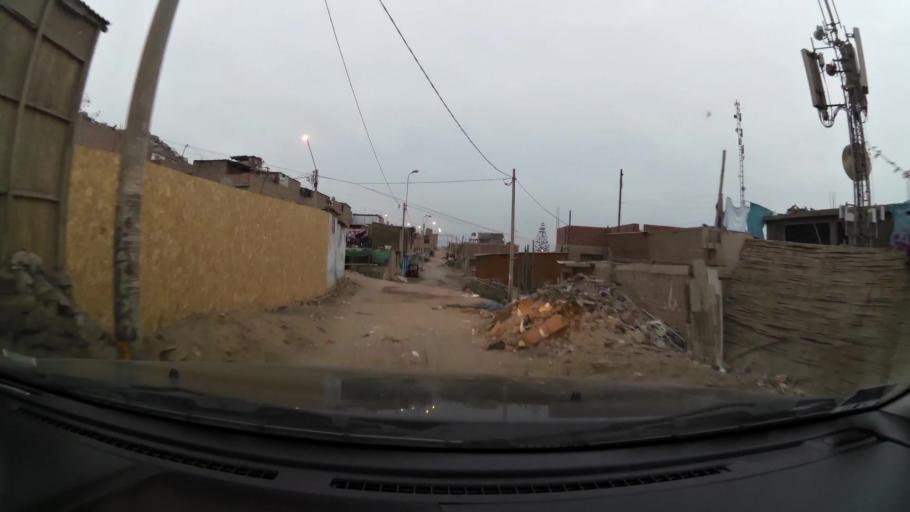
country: PE
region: Lima
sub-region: Lima
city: Surco
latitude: -12.1939
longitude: -77.0262
